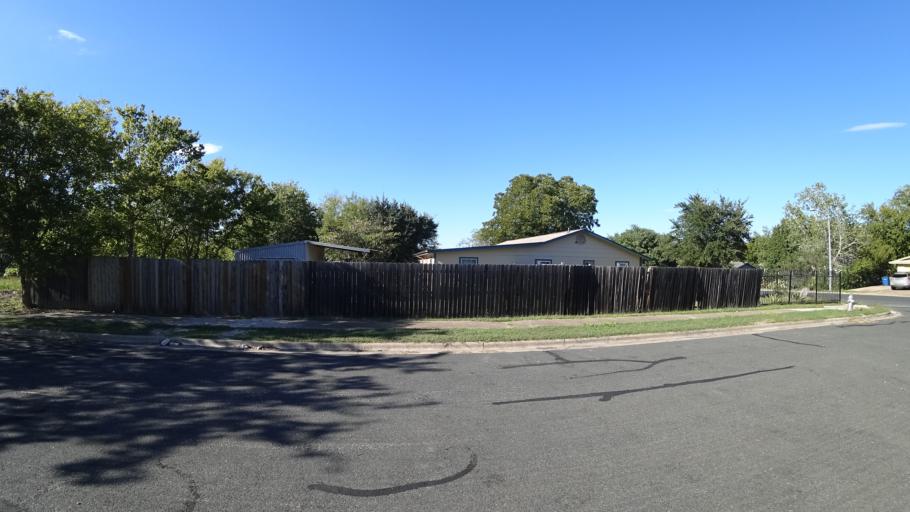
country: US
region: Texas
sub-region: Travis County
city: Hornsby Bend
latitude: 30.2976
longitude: -97.6293
